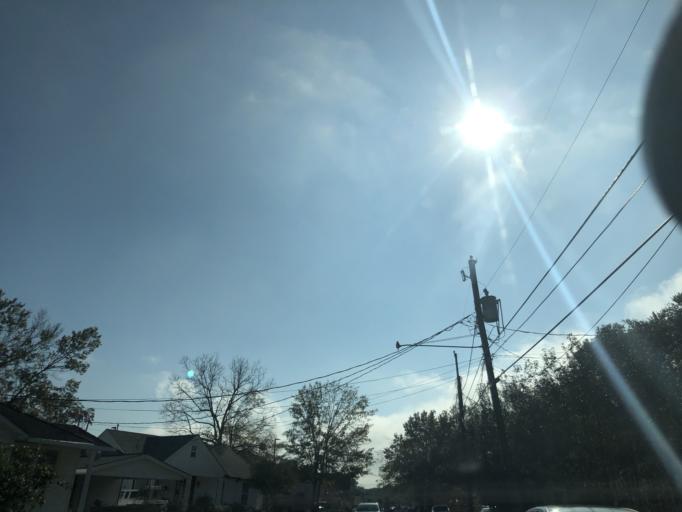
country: US
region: Louisiana
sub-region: Jefferson Parish
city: Metairie
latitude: 29.9815
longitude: -90.1521
